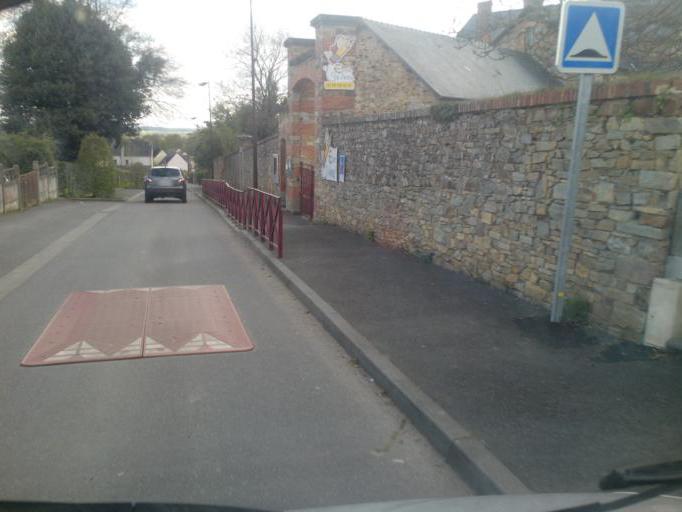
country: FR
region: Brittany
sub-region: Departement d'Ille-et-Vilaine
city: Grand-Fougeray
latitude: 47.7260
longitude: -1.7341
